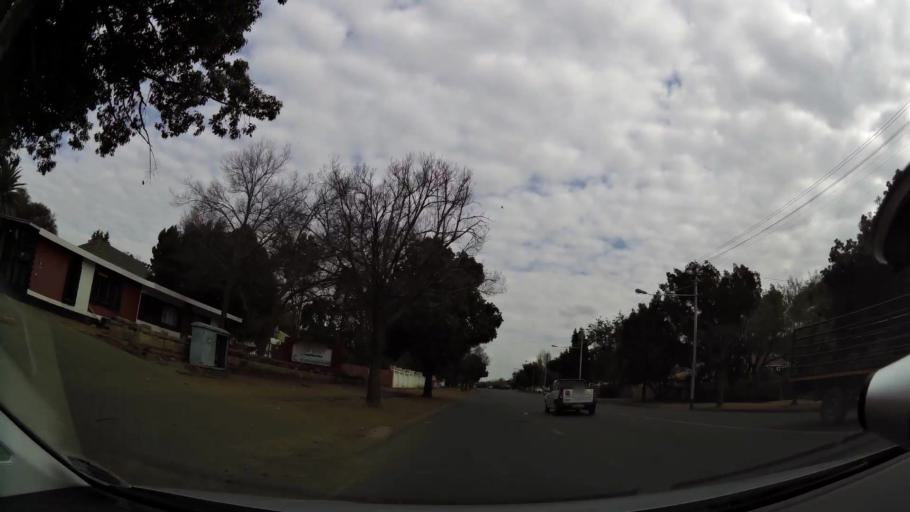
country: ZA
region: Orange Free State
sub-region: Mangaung Metropolitan Municipality
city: Bloemfontein
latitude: -29.0965
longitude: 26.2251
